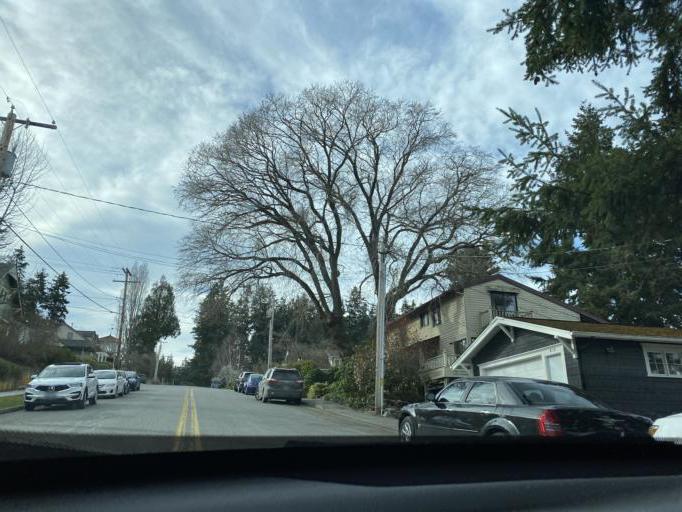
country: US
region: Washington
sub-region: Island County
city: Langley
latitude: 48.0409
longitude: -122.4113
